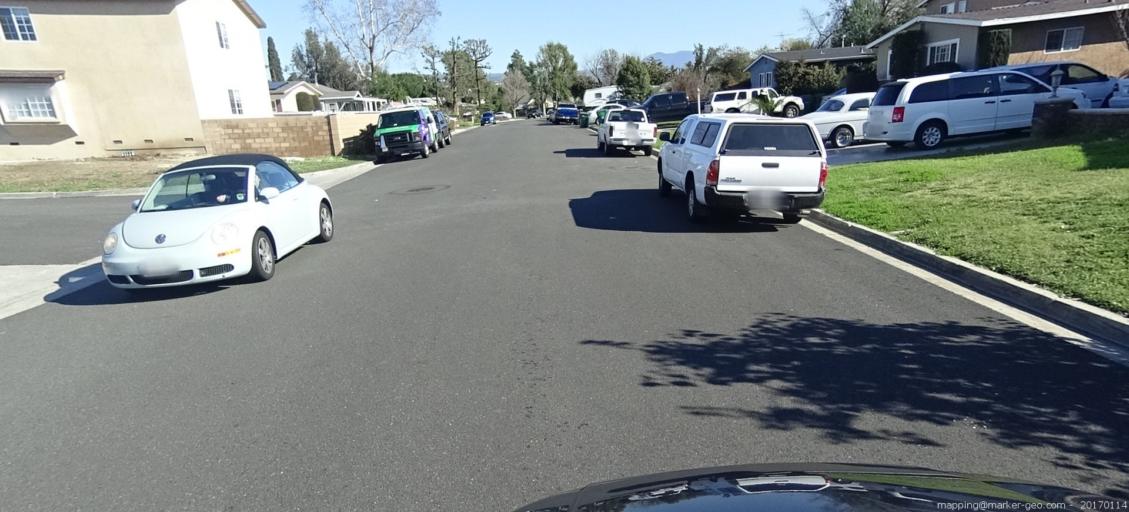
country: US
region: California
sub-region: Orange County
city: Tustin
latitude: 33.7557
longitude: -117.8171
